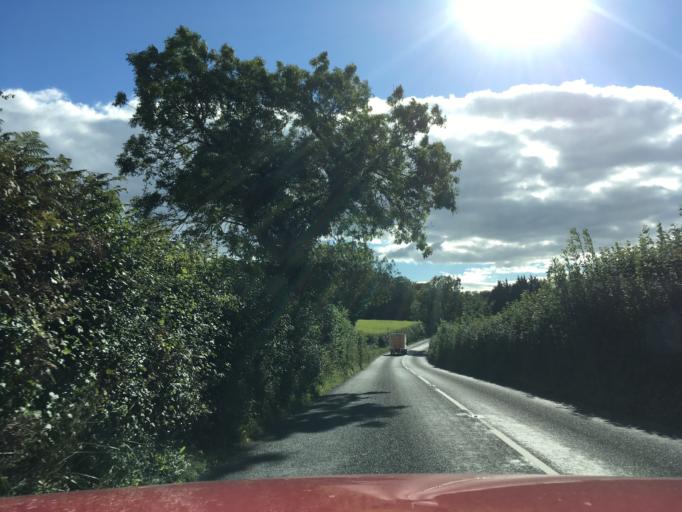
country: GB
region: England
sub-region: Devon
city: Buckfastleigh
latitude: 50.4360
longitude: -3.7434
